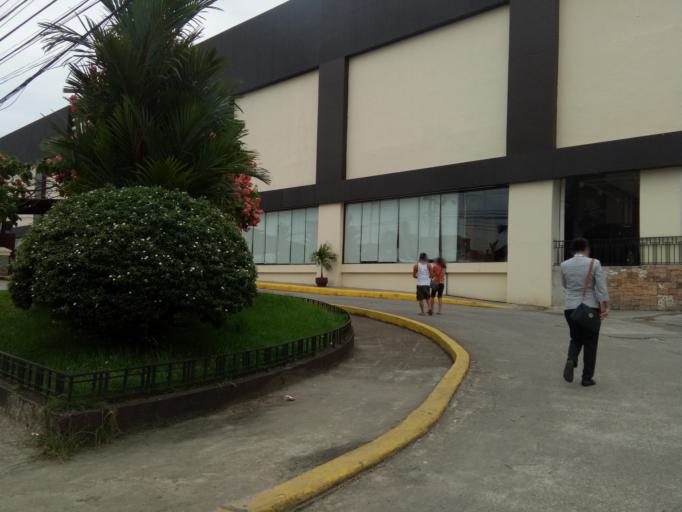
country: PH
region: Caraga
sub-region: Province of Surigao del Norte
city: Rizal
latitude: 9.7637
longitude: 125.4832
